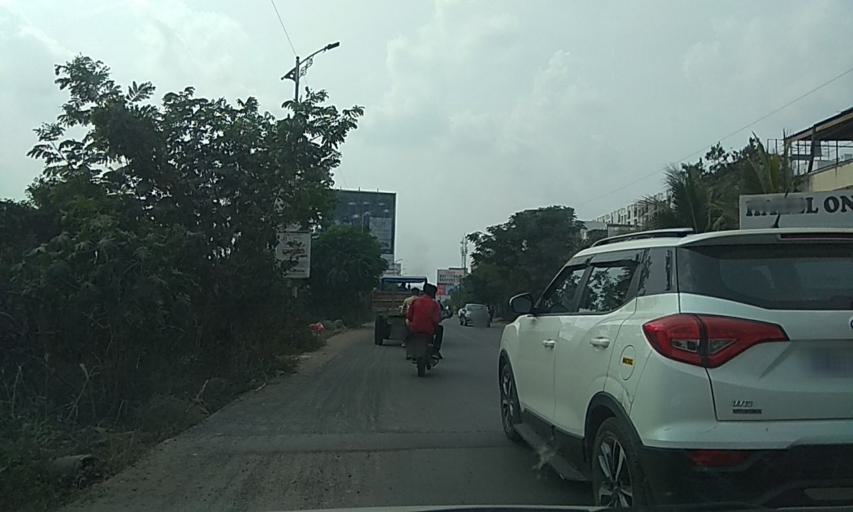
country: IN
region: Maharashtra
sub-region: Pune Division
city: Pimpri
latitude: 18.5831
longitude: 73.7286
